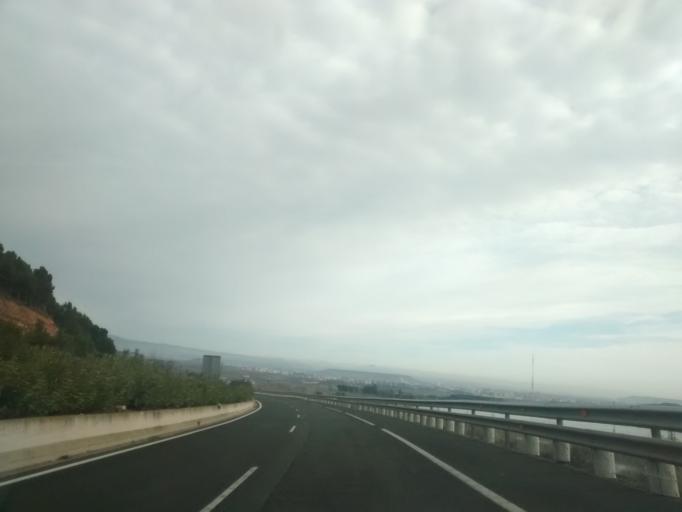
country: ES
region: La Rioja
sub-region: Provincia de La Rioja
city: Navarrete
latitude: 42.4409
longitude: -2.5216
